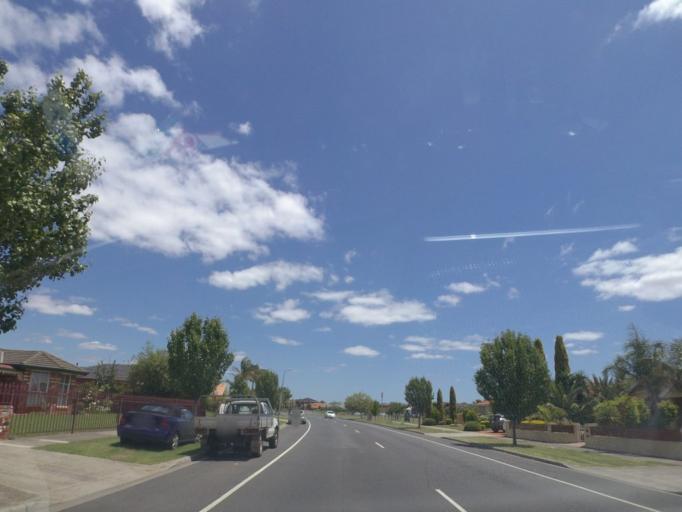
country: AU
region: Victoria
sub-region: Brimbank
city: Sunshine West
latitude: -37.7970
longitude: 144.7941
